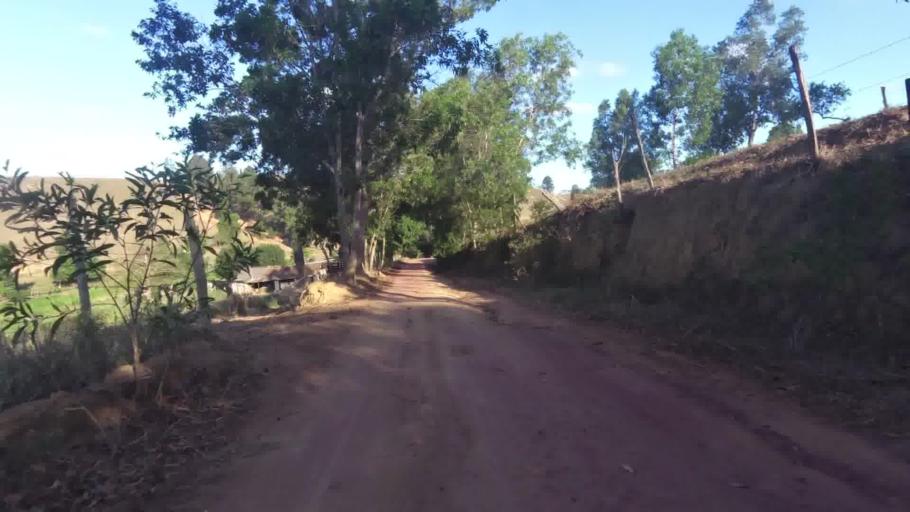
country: BR
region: Espirito Santo
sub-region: Marataizes
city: Marataizes
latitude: -21.1648
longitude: -41.0531
